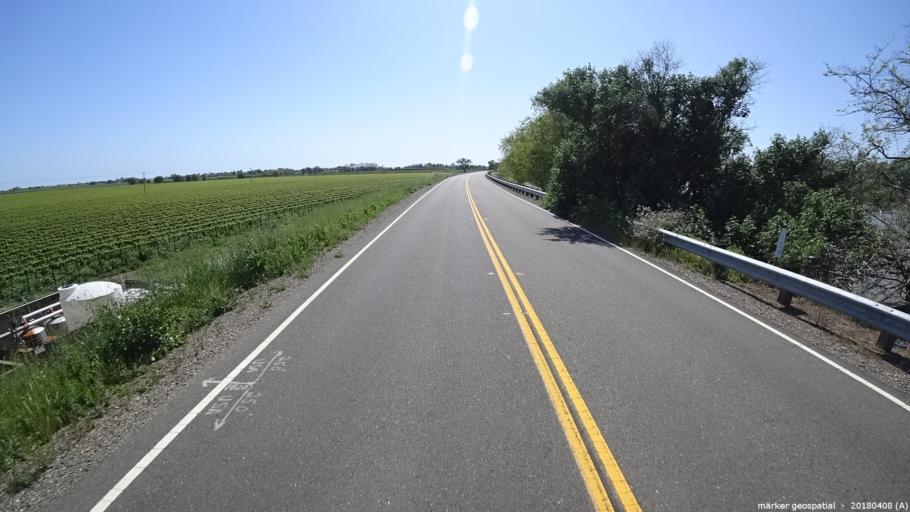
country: US
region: California
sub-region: Sacramento County
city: Laguna
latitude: 38.3848
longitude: -121.5154
